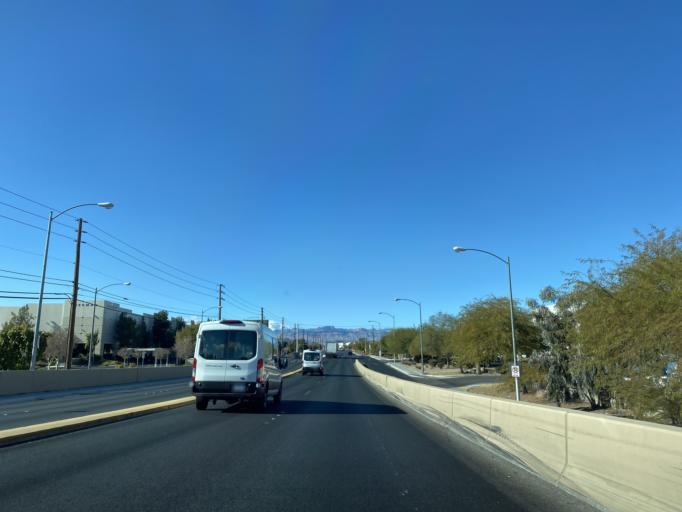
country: US
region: Nevada
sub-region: Clark County
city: Paradise
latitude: 36.0710
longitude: -115.1827
